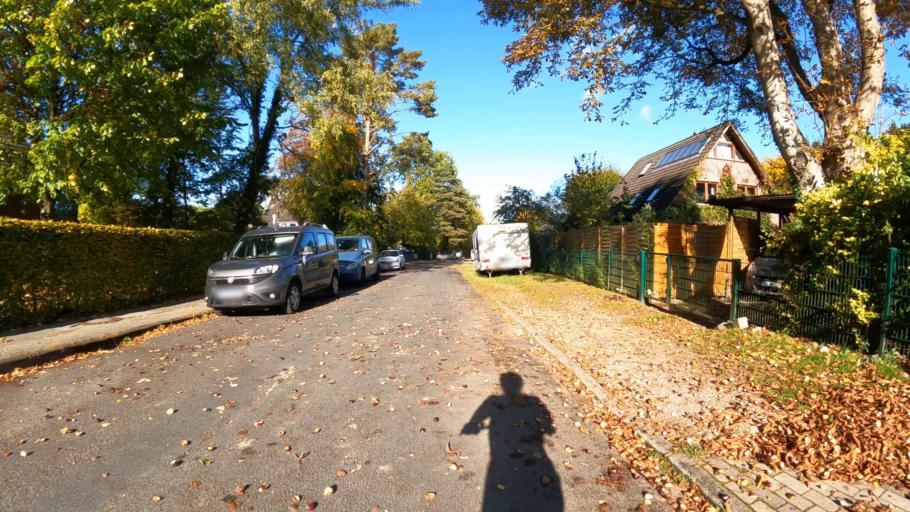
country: DE
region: Schleswig-Holstein
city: Grosshansdorf
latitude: 53.6588
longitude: 10.2530
